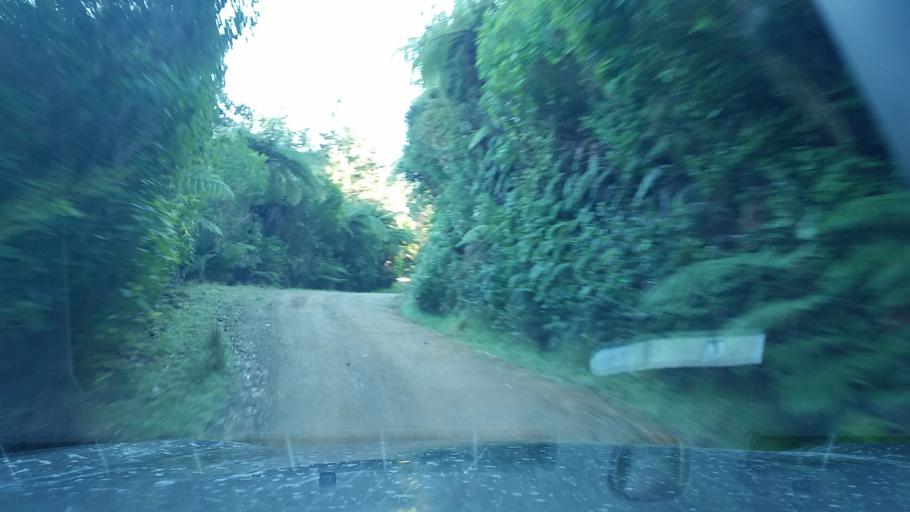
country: NZ
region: Marlborough
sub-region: Marlborough District
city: Picton
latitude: -41.1225
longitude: 173.9900
